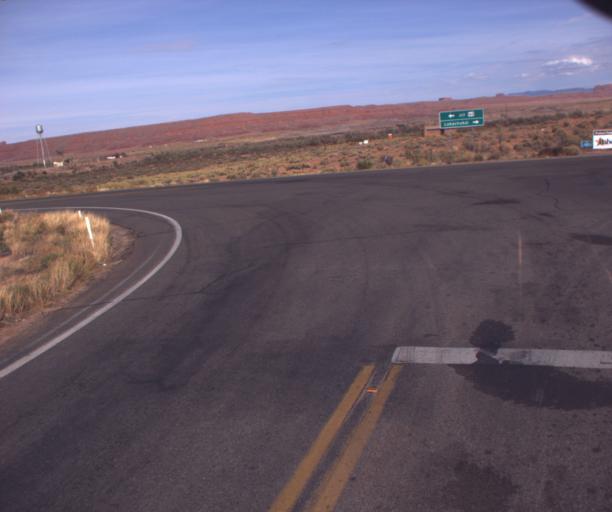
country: US
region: Arizona
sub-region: Apache County
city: Many Farms
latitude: 36.5088
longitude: -109.4727
